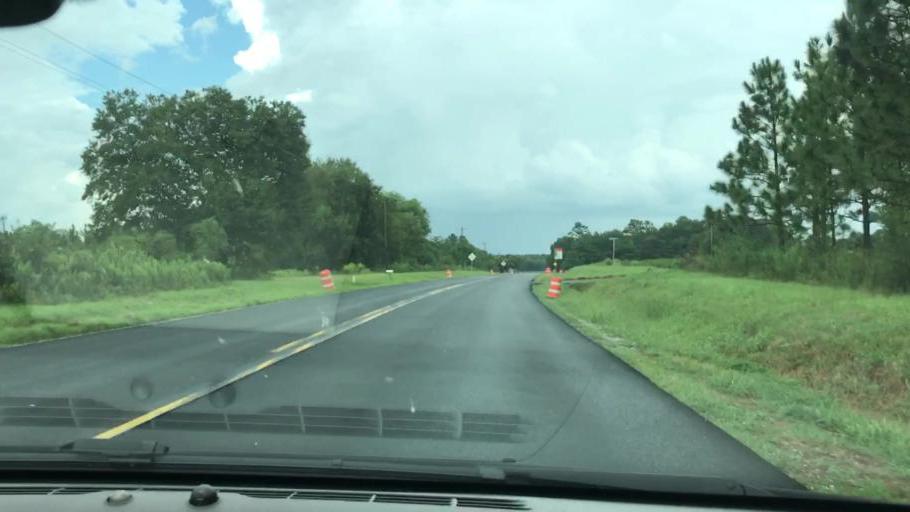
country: US
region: Georgia
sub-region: Early County
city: Blakely
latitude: 31.4159
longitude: -84.9628
